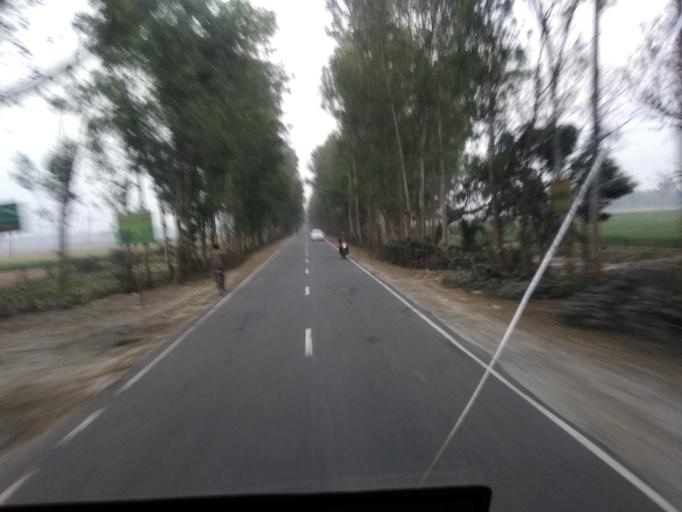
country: BD
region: Rajshahi
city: Bogra
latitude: 24.6687
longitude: 89.2756
